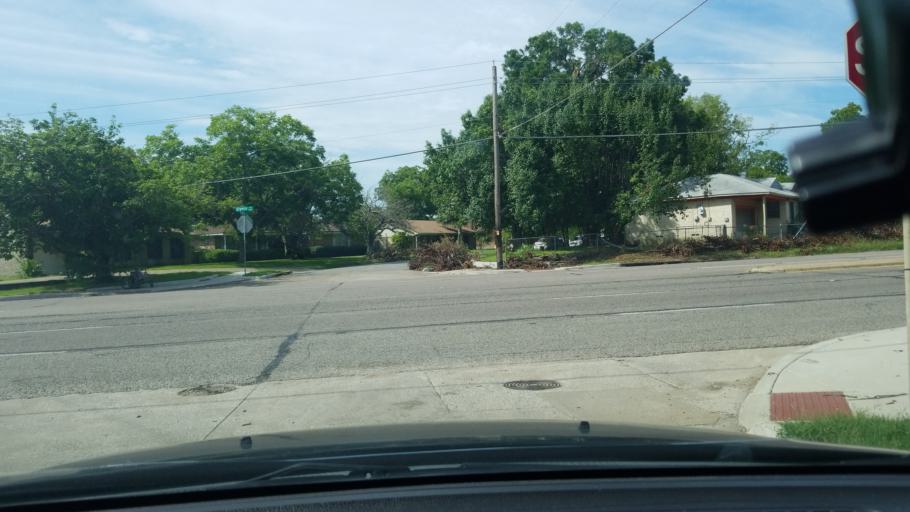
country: US
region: Texas
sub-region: Dallas County
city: Balch Springs
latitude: 32.7636
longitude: -96.6701
